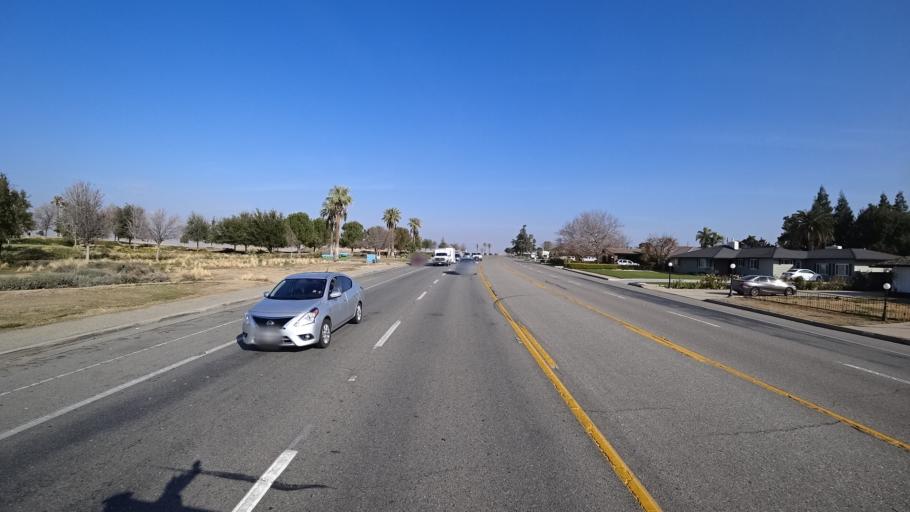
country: US
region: California
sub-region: Kern County
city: Oildale
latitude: 35.4079
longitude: -118.9924
